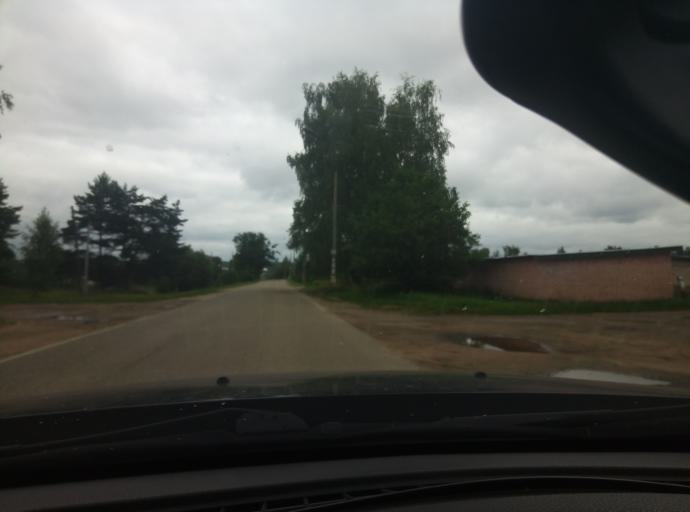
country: RU
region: Kaluga
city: Zhukovo
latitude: 54.9583
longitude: 36.7881
